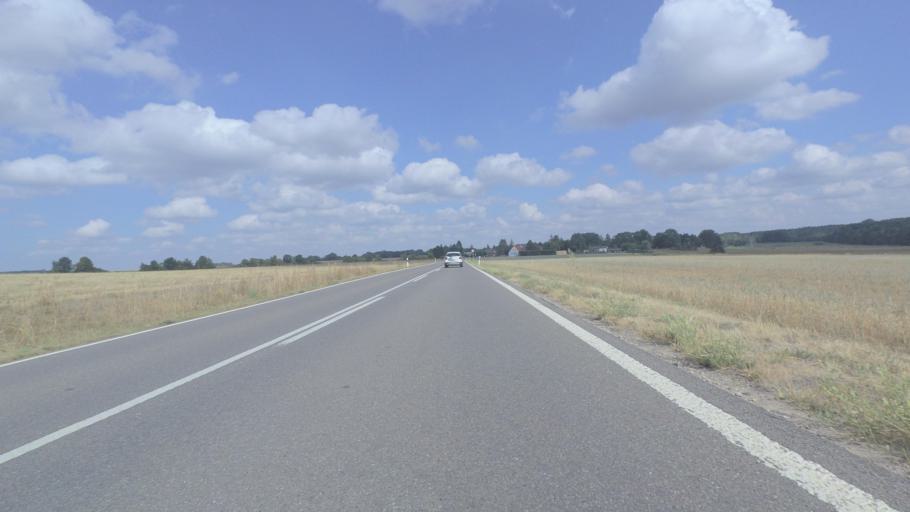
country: DE
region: Brandenburg
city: Walsleben
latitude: 53.0056
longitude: 12.6477
